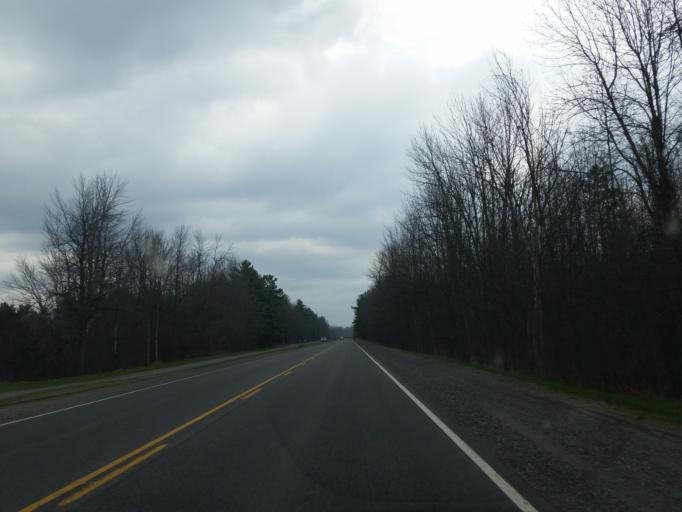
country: CA
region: Ontario
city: Brockville
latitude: 44.4939
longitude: -75.8140
